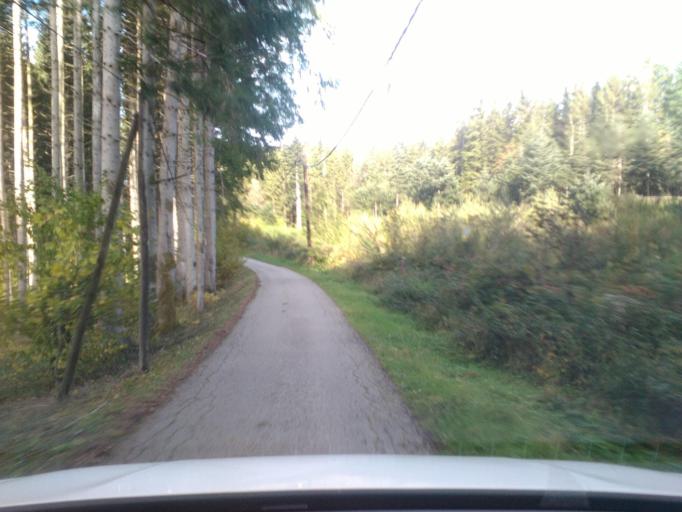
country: FR
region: Lorraine
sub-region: Departement des Vosges
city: Senones
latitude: 48.4062
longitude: 7.0728
